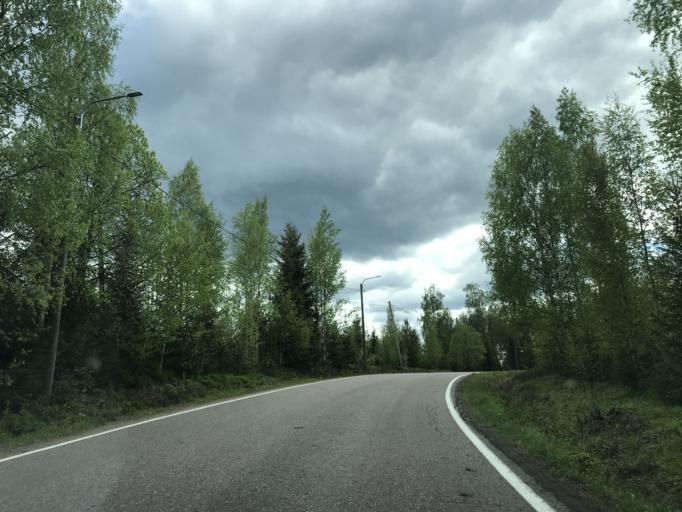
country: FI
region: Uusimaa
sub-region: Helsinki
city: Vihti
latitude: 60.4369
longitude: 24.5225
